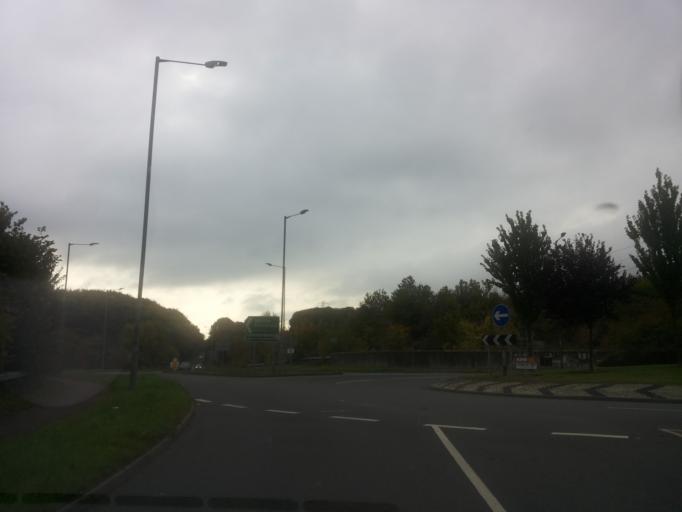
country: GB
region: England
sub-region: Buckinghamshire
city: Wendover
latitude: 51.7538
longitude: -0.7370
